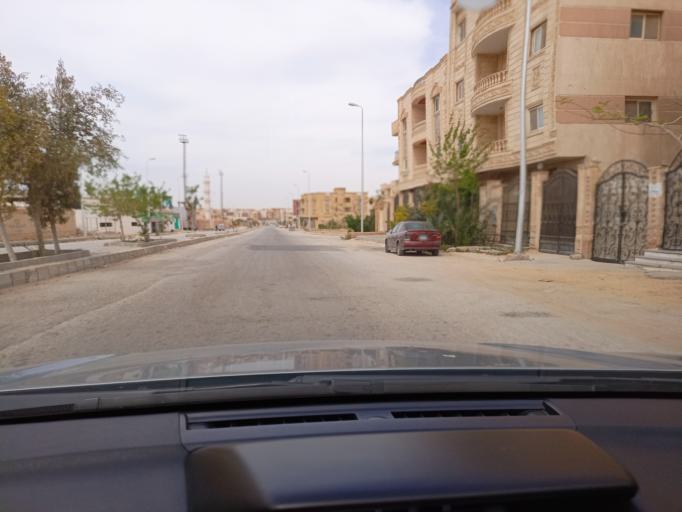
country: EG
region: Muhafazat al Qalyubiyah
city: Al Khankah
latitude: 30.2482
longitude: 31.4970
